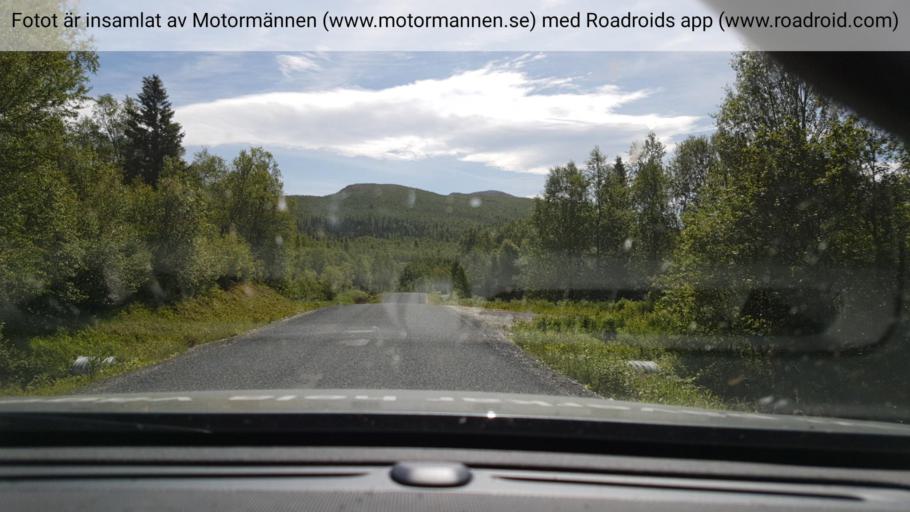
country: SE
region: Vaesterbotten
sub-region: Vilhelmina Kommun
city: Sjoberg
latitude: 65.3189
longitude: 15.2862
